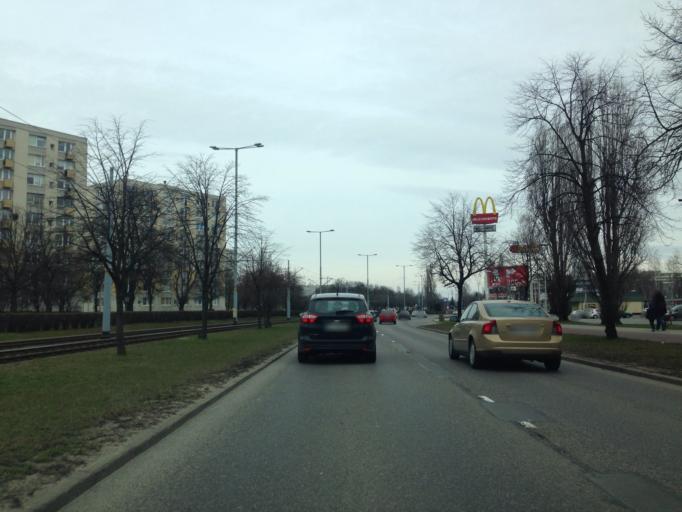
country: PL
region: Pomeranian Voivodeship
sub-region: Sopot
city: Sopot
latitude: 54.4061
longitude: 18.5902
